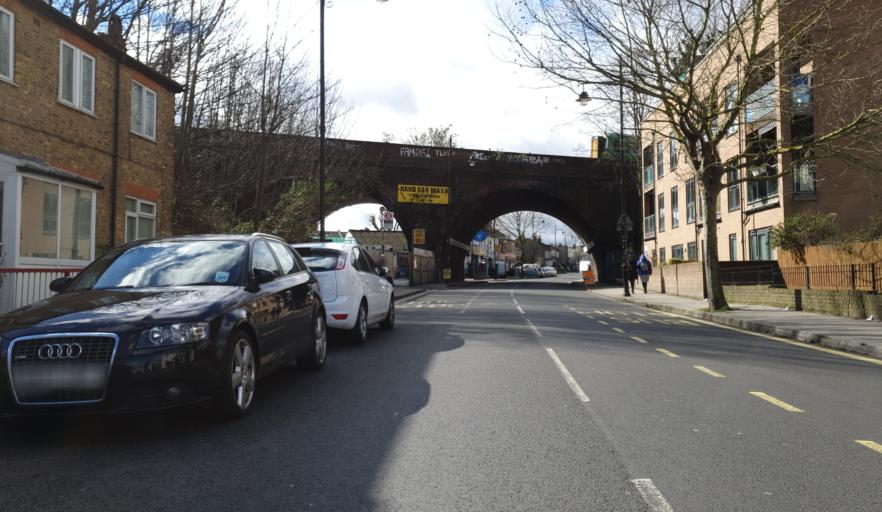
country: GB
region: England
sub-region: Greater London
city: Camberwell
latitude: 51.4676
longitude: -0.0540
